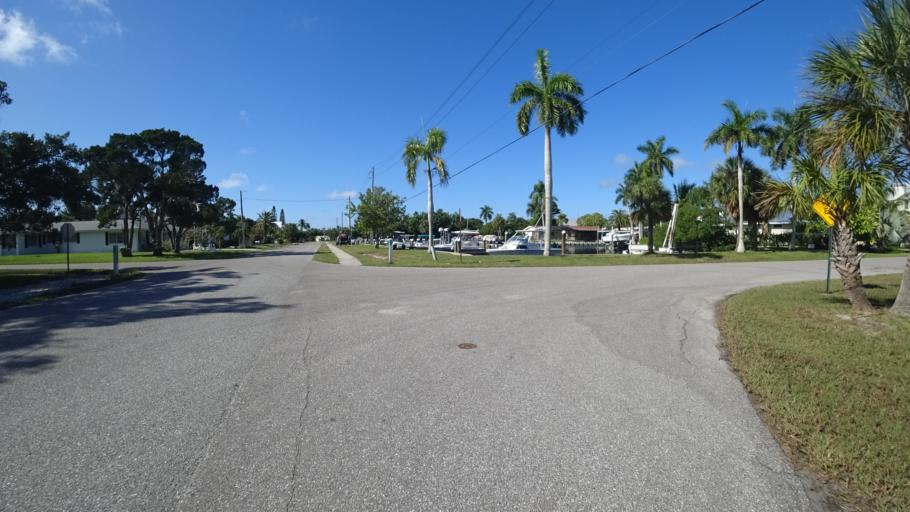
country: US
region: Florida
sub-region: Manatee County
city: Anna Maria
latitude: 27.5190
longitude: -82.7224
